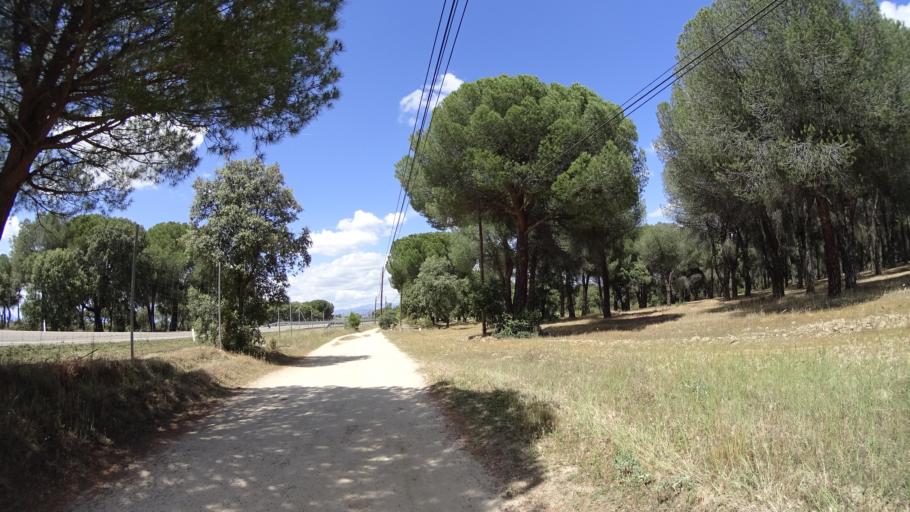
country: ES
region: Madrid
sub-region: Provincia de Madrid
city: Boadilla del Monte
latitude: 40.4368
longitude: -3.8763
